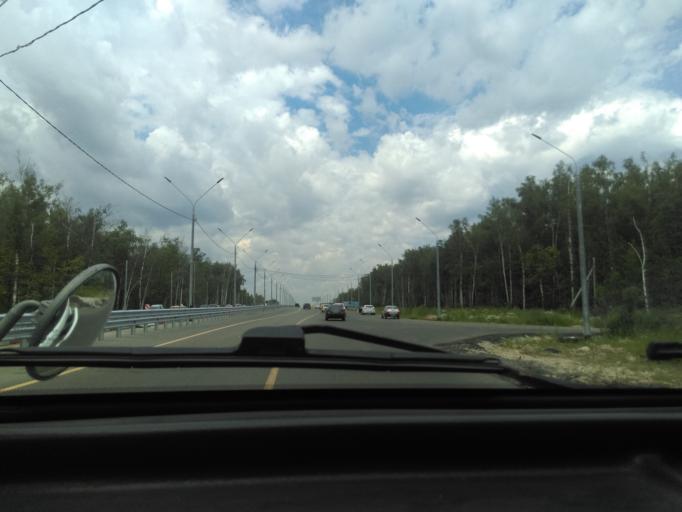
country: RU
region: Moskovskaya
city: Yakovlevskoye
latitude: 55.4245
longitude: 37.8881
